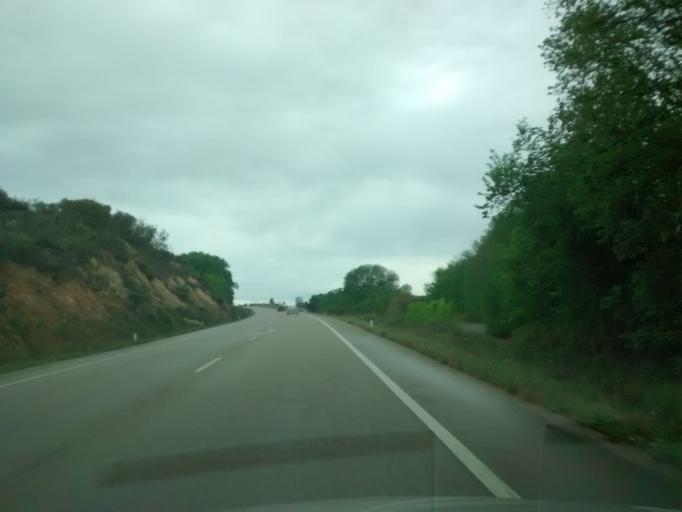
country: ES
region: Aragon
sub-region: Provincia de Zaragoza
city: Caspe
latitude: 41.2147
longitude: 0.0016
